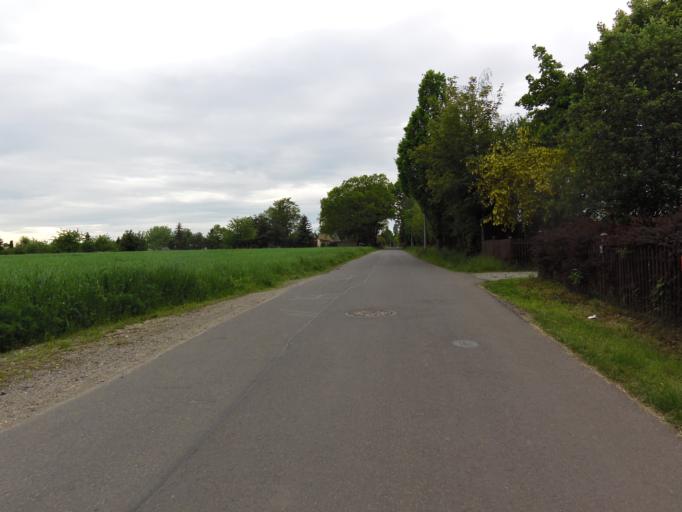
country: DE
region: Saxony
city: Markkleeberg
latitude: 51.2794
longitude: 12.3082
